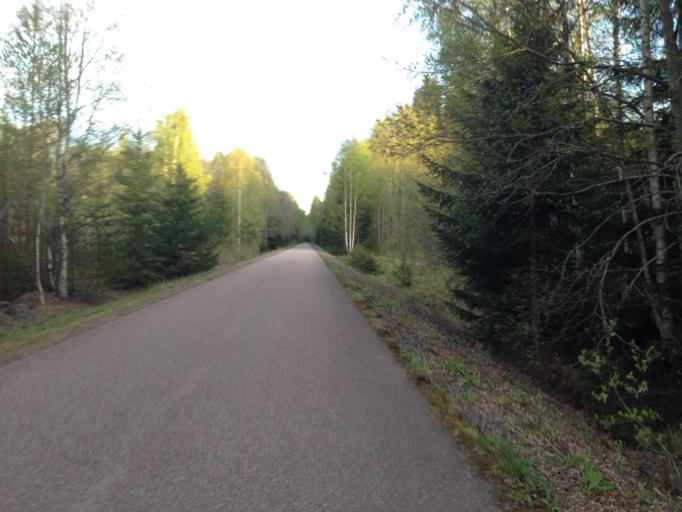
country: SE
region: Dalarna
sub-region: Ludvika Kommun
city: Grangesberg
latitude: 60.1301
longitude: 15.0703
